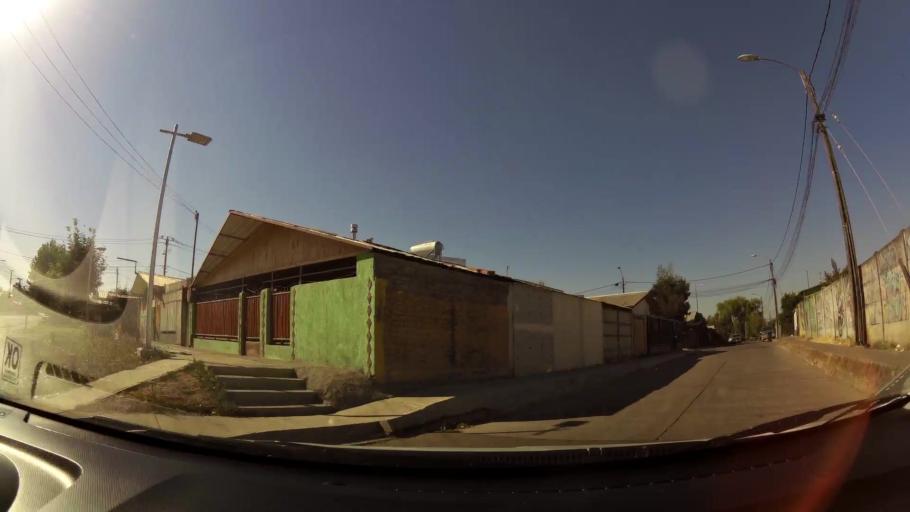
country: CL
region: Maule
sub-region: Provincia de Curico
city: Curico
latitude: -34.9990
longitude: -71.2489
